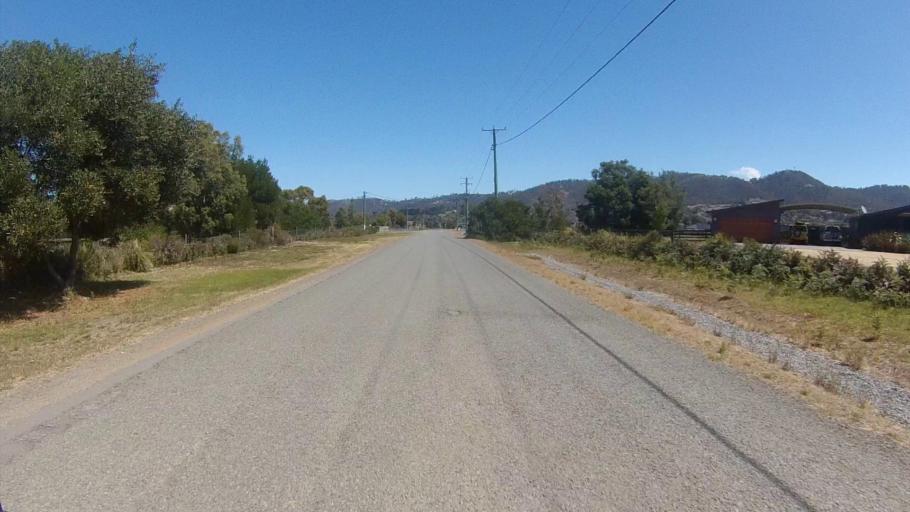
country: AU
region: Tasmania
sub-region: Clarence
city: Seven Mile Beach
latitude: -42.8507
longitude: 147.4922
